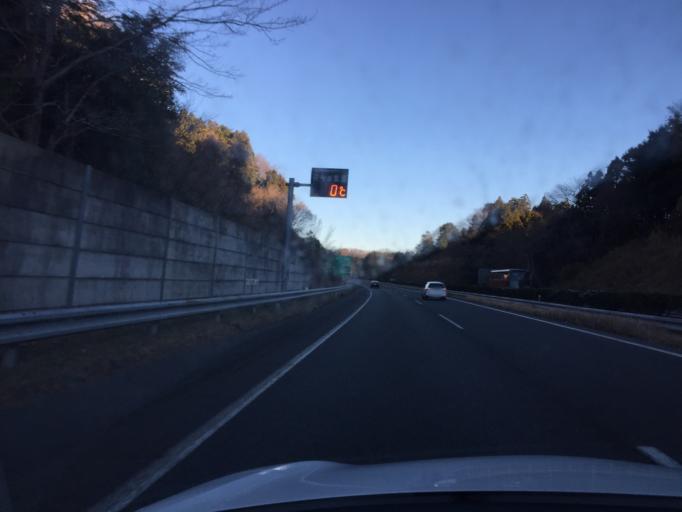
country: JP
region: Fukushima
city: Iwaki
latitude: 37.0116
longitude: 140.8142
